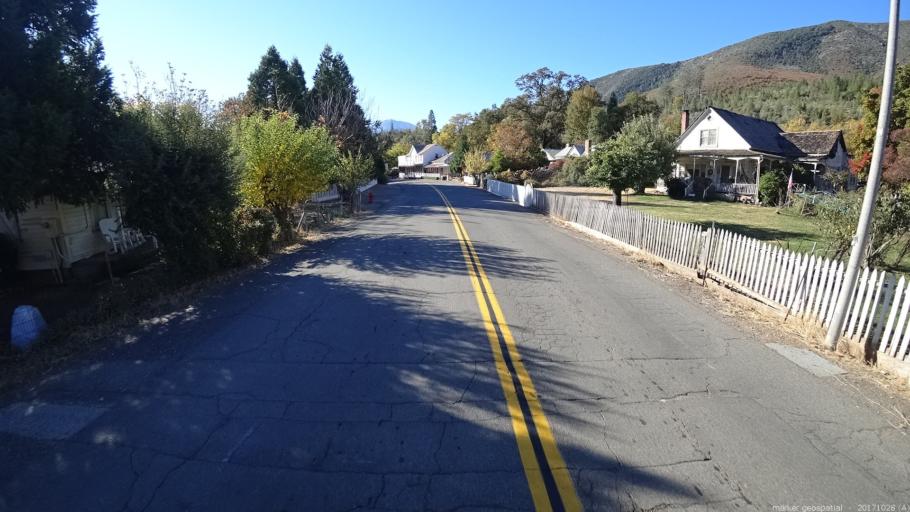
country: US
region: California
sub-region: Trinity County
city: Lewiston
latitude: 40.7003
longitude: -122.6386
